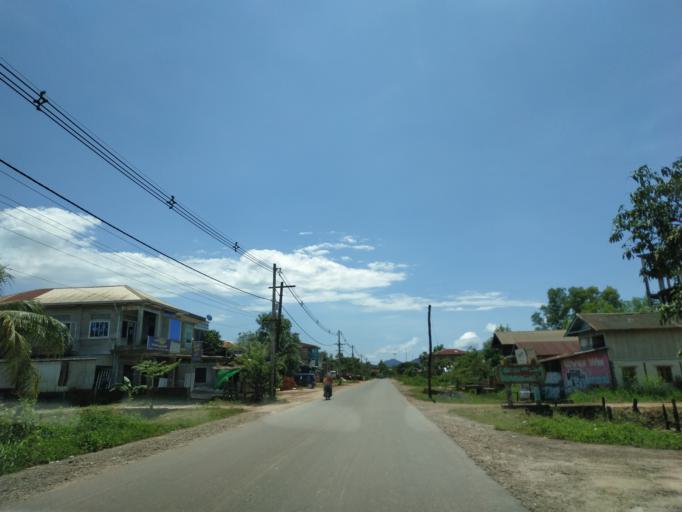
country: MM
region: Tanintharyi
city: Dawei
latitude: 14.0929
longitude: 98.1852
